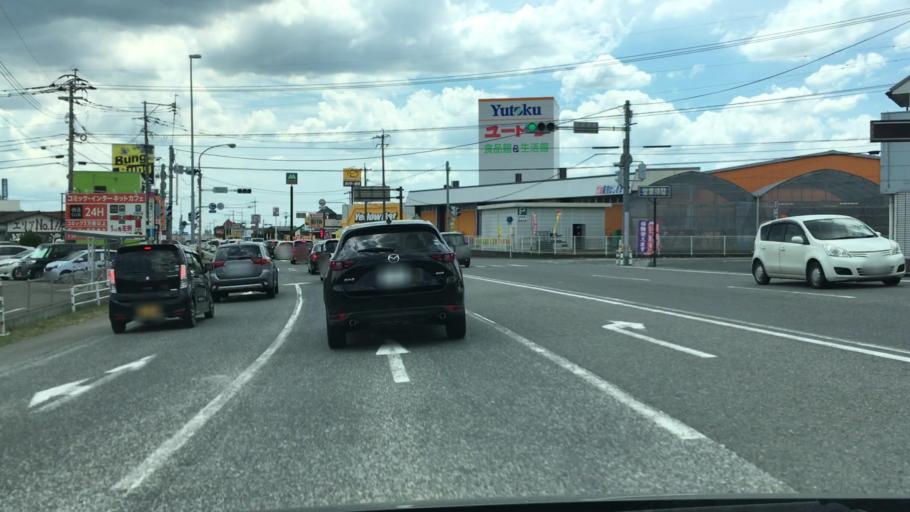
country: JP
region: Saga Prefecture
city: Tosu
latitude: 33.3897
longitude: 130.5001
